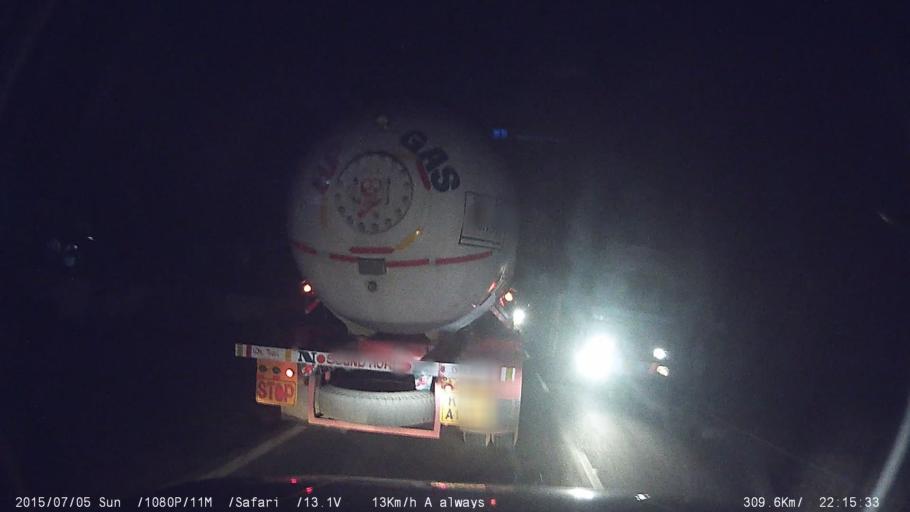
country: IN
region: Kerala
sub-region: Palakkad district
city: Palakkad
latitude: 10.8630
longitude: 76.5598
